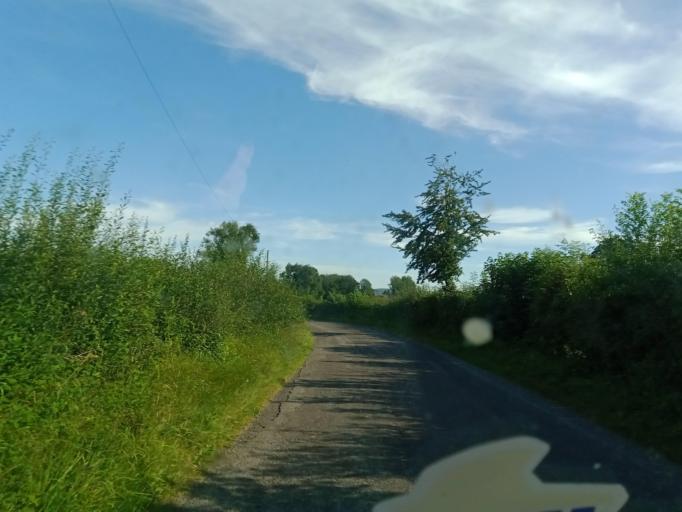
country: IE
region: Leinster
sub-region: Kilkenny
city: Ballyragget
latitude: 52.7664
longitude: -7.3915
